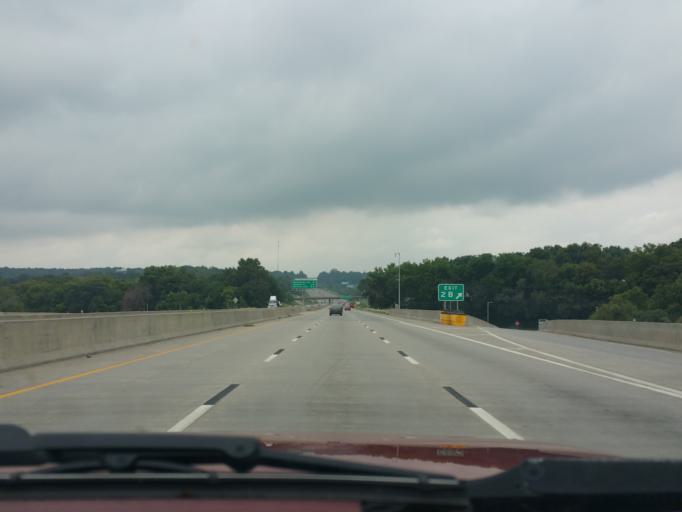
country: US
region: Kansas
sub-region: Johnson County
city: Shawnee
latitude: 39.0814
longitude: -94.6807
